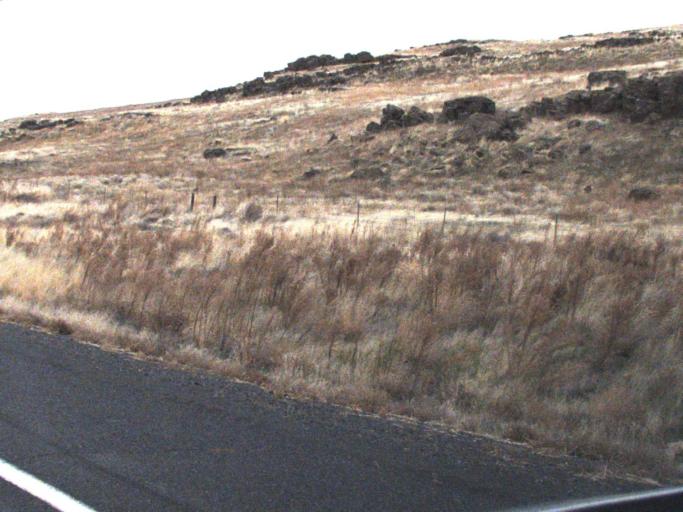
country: US
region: Washington
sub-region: Columbia County
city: Dayton
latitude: 46.7760
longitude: -118.0528
